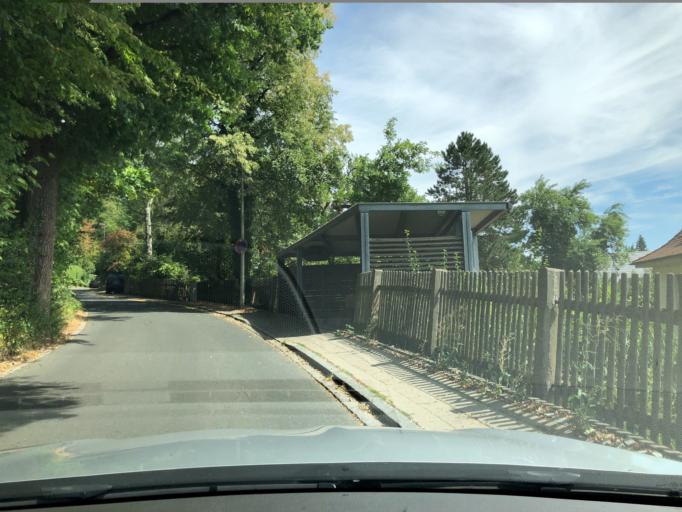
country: DE
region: Bavaria
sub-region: Regierungsbezirk Mittelfranken
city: Ruckersdorf
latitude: 49.5033
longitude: 11.2573
